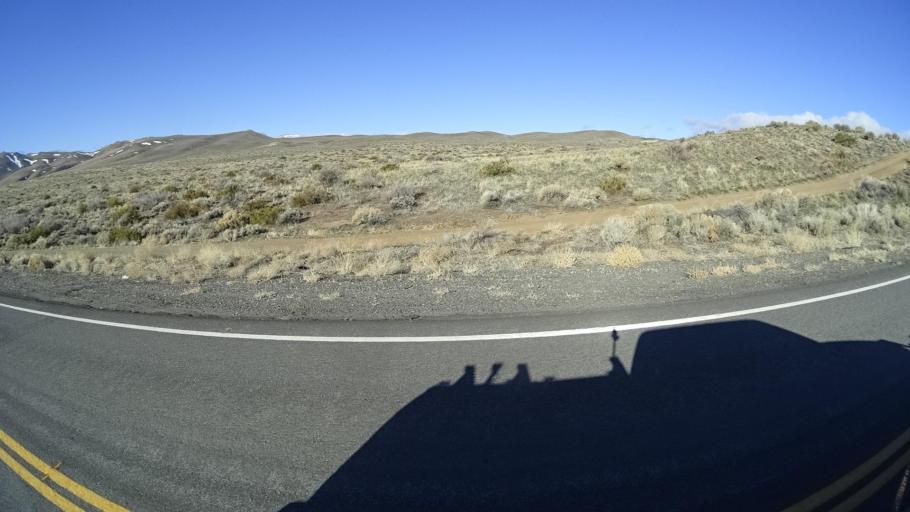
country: US
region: Nevada
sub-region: Washoe County
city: Cold Springs
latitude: 39.6767
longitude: -119.9224
